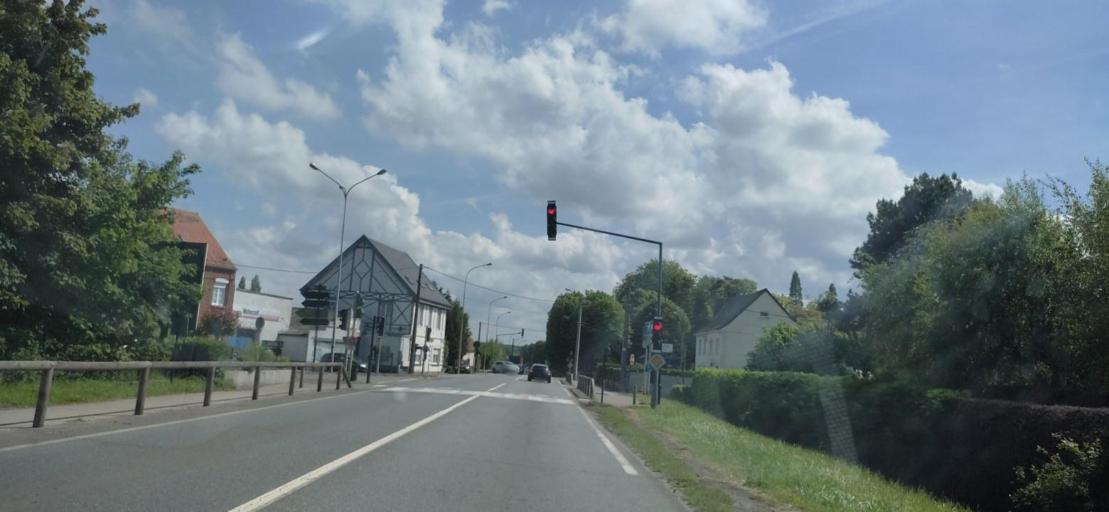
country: FR
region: Nord-Pas-de-Calais
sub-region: Departement du Pas-de-Calais
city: Aire-sur-la-Lys
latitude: 50.6332
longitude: 2.3896
